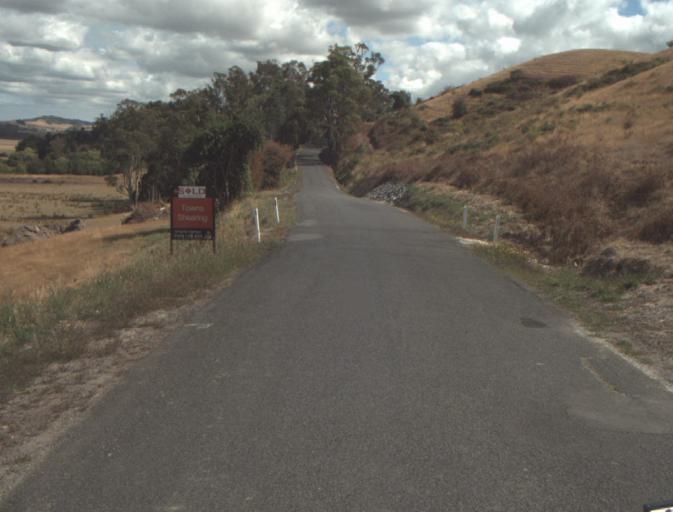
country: AU
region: Tasmania
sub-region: Launceston
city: Mayfield
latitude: -41.2420
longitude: 147.1497
